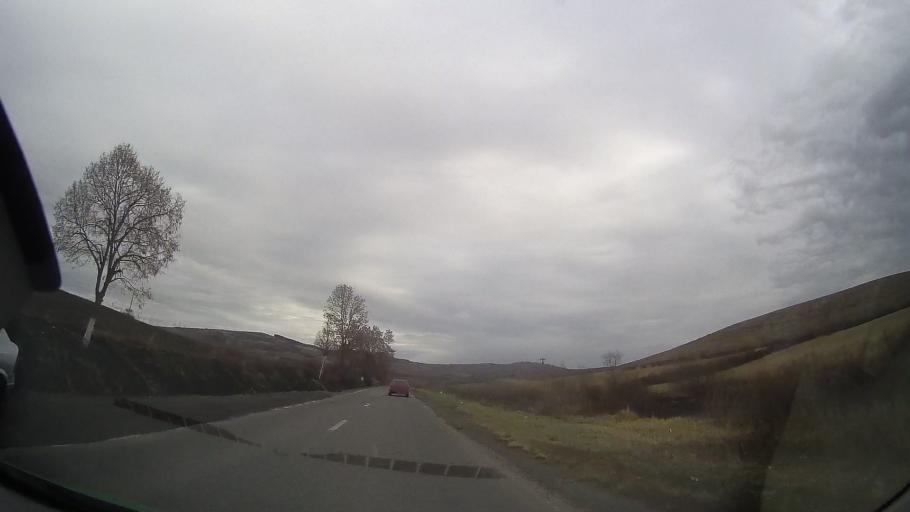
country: RO
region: Mures
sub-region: Comuna Faragau
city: Faragau
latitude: 46.7642
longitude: 24.5494
